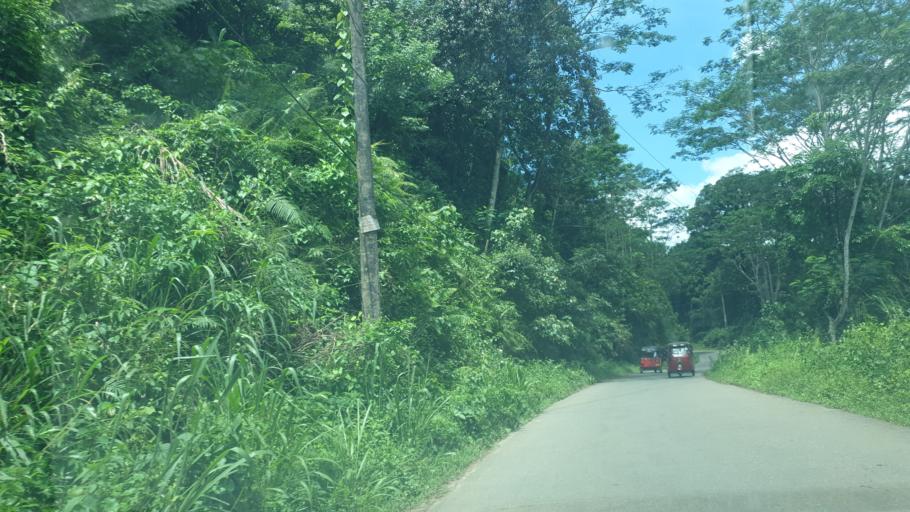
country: LK
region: Sabaragamuwa
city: Ratnapura
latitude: 6.4834
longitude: 80.4089
